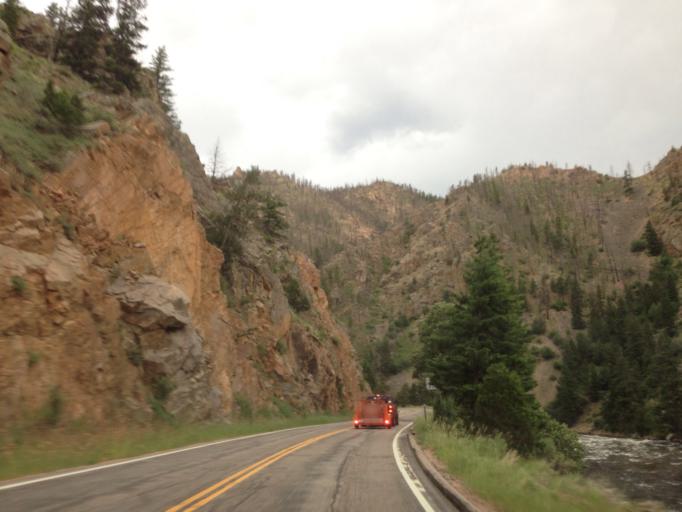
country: US
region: Colorado
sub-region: Larimer County
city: Laporte
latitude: 40.6828
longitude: -105.4344
